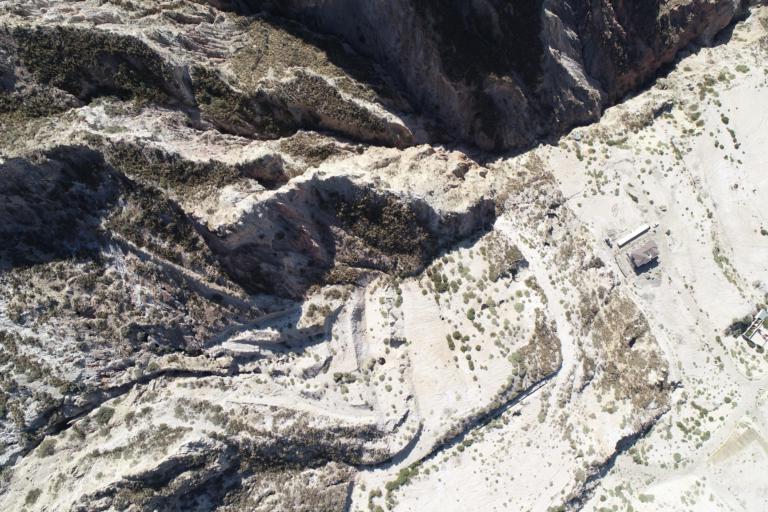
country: BO
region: La Paz
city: La Paz
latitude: -16.5540
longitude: -68.1068
